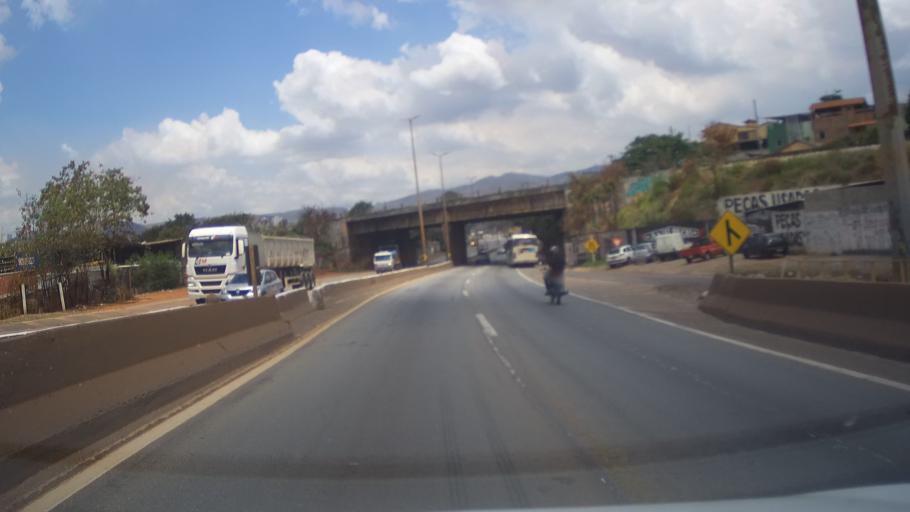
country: BR
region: Minas Gerais
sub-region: Contagem
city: Contagem
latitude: -19.9555
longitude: -44.0034
